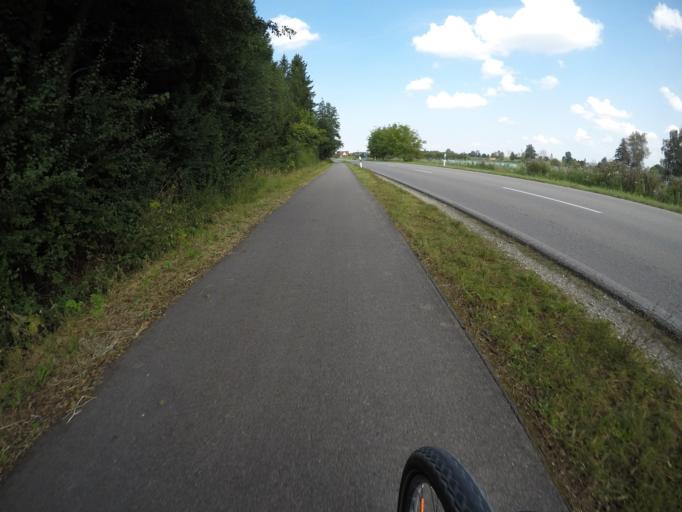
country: DE
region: Bavaria
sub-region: Swabia
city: Kuhlenthal
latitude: 48.5561
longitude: 10.8193
